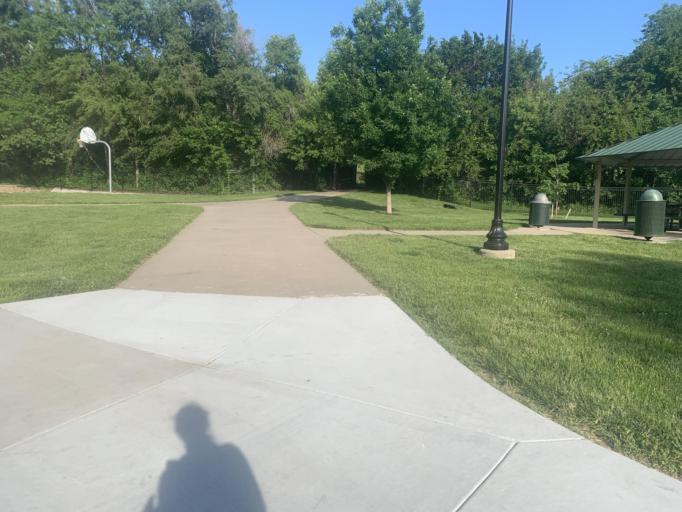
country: US
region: Nebraska
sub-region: Douglas County
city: Ralston
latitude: 41.1843
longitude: -96.0691
